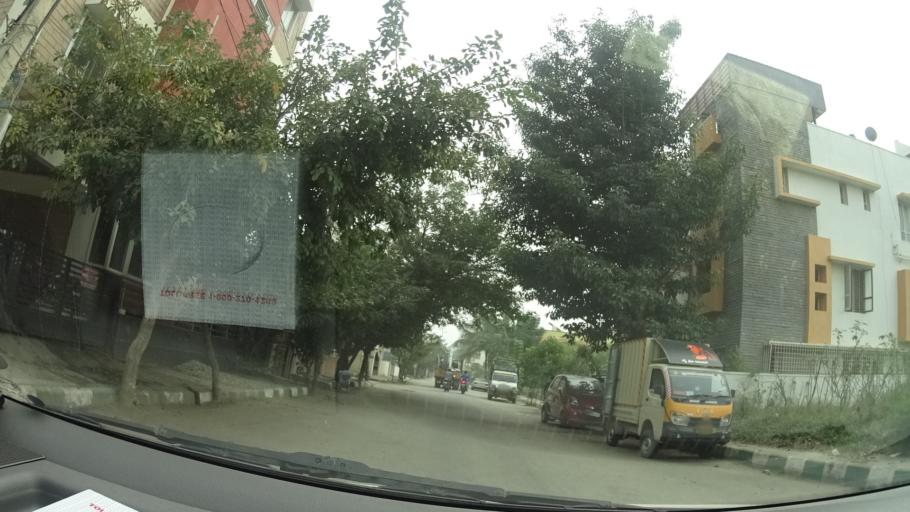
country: IN
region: Karnataka
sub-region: Bangalore Urban
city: Yelahanka
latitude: 13.0402
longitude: 77.6261
